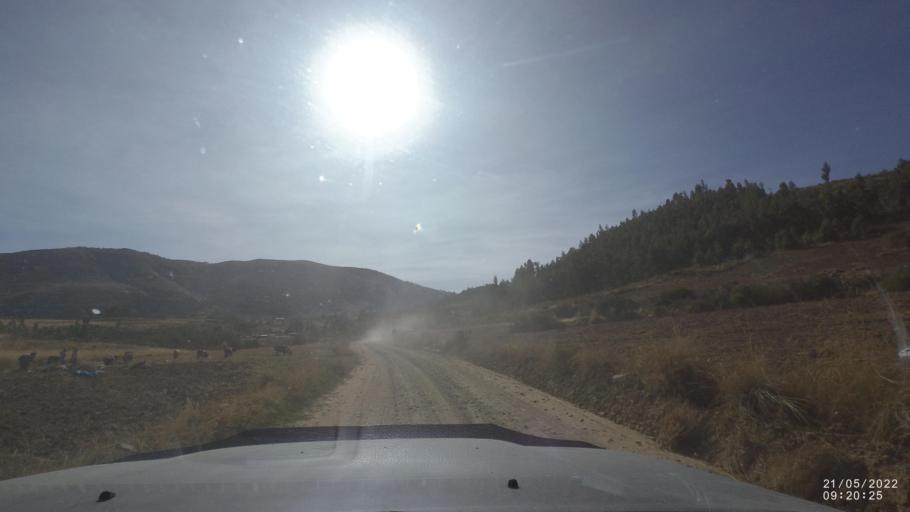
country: BO
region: Cochabamba
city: Cochabamba
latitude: -17.3556
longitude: -66.0215
